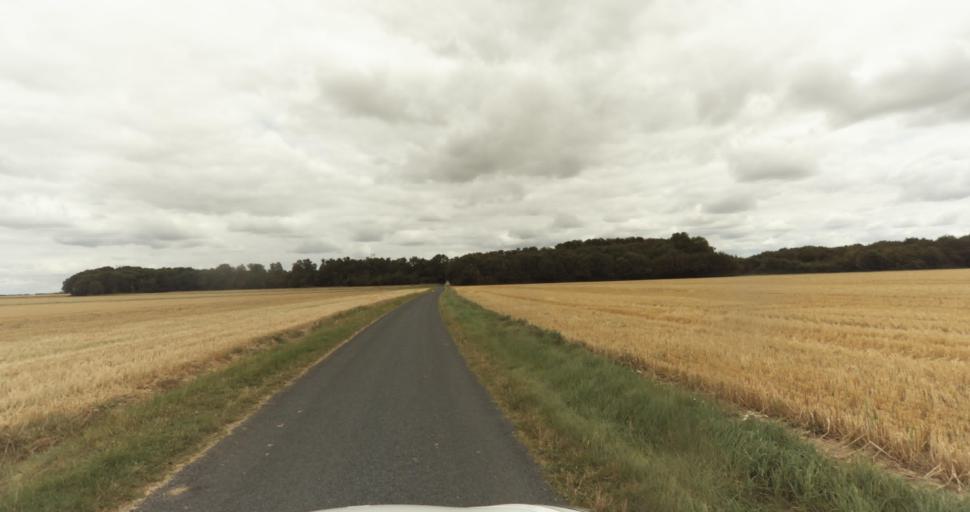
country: FR
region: Haute-Normandie
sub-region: Departement de l'Eure
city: La Madeleine-de-Nonancourt
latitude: 48.8421
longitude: 1.2028
